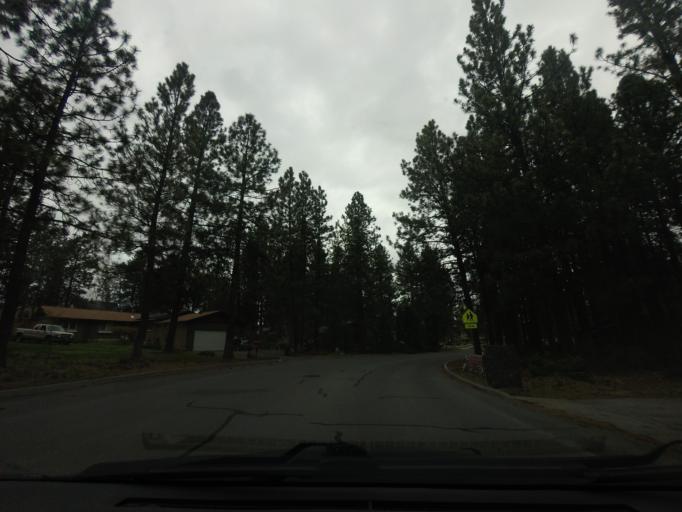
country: US
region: Oregon
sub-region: Deschutes County
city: Bend
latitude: 44.0224
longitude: -121.3299
